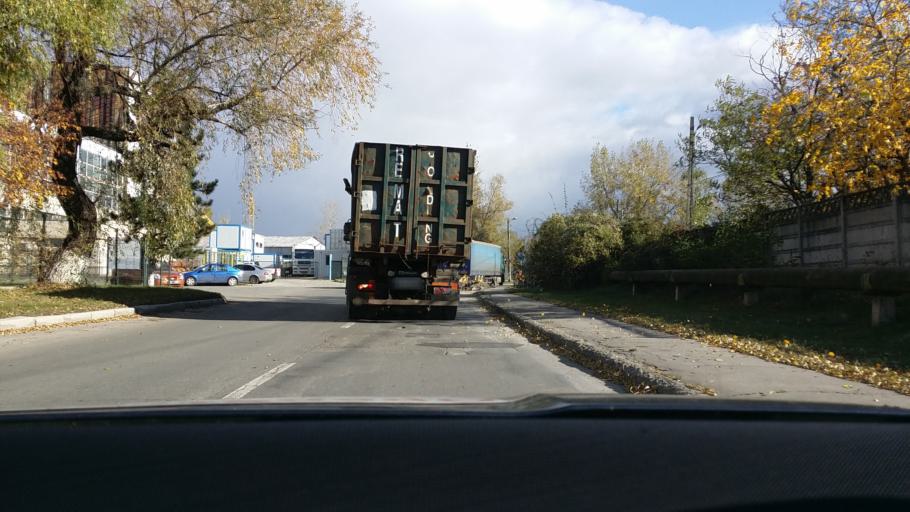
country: RO
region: Prahova
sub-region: Municipiul Campina
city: Campina
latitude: 45.1225
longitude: 25.7471
